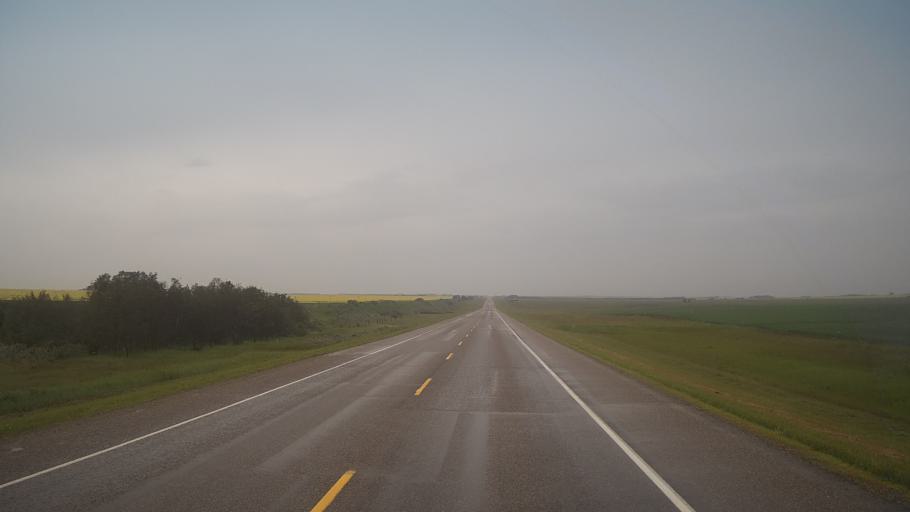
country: CA
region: Saskatchewan
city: Wilkie
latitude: 52.2122
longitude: -108.4947
